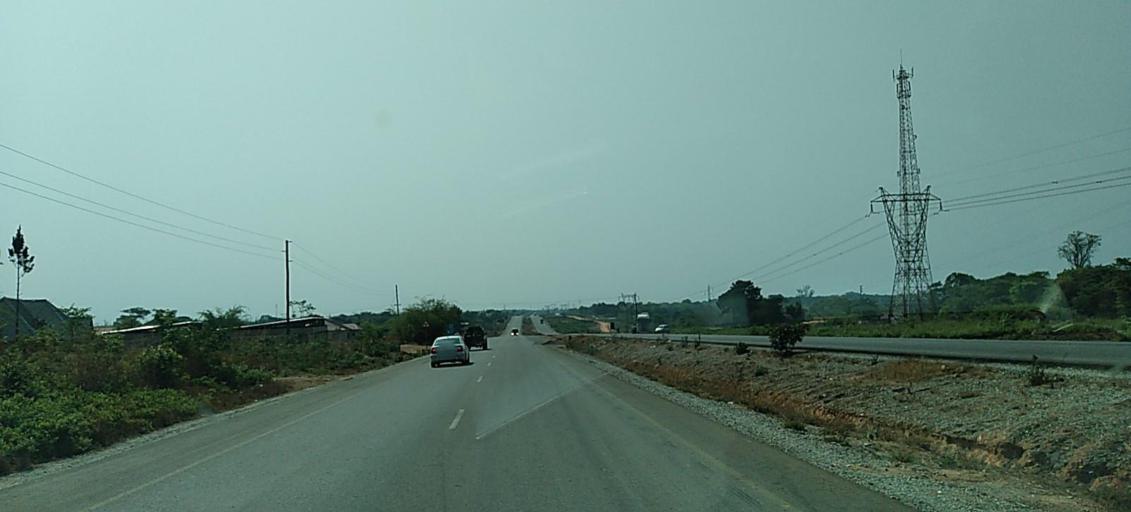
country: ZM
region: Copperbelt
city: Chingola
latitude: -12.5949
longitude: 27.9556
